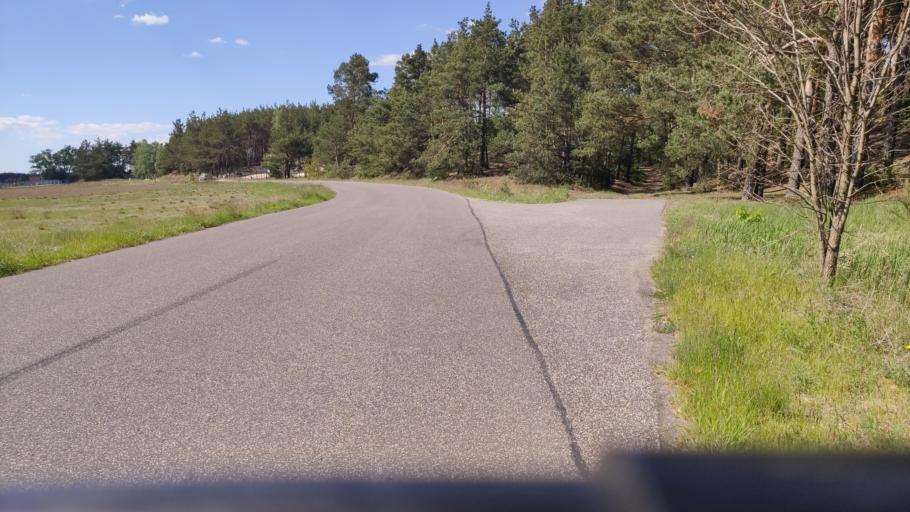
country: PL
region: Kujawsko-Pomorskie
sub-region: Wloclawek
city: Wloclawek
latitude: 52.5829
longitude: 19.0959
